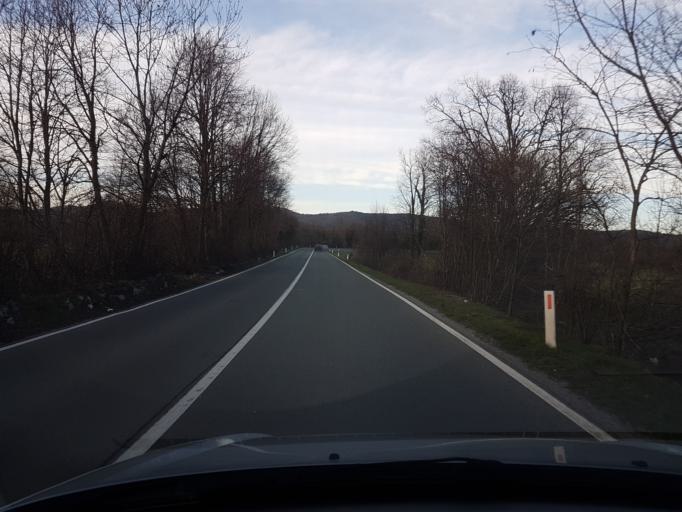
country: SI
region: Sezana
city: Sezana
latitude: 45.6598
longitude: 13.9044
